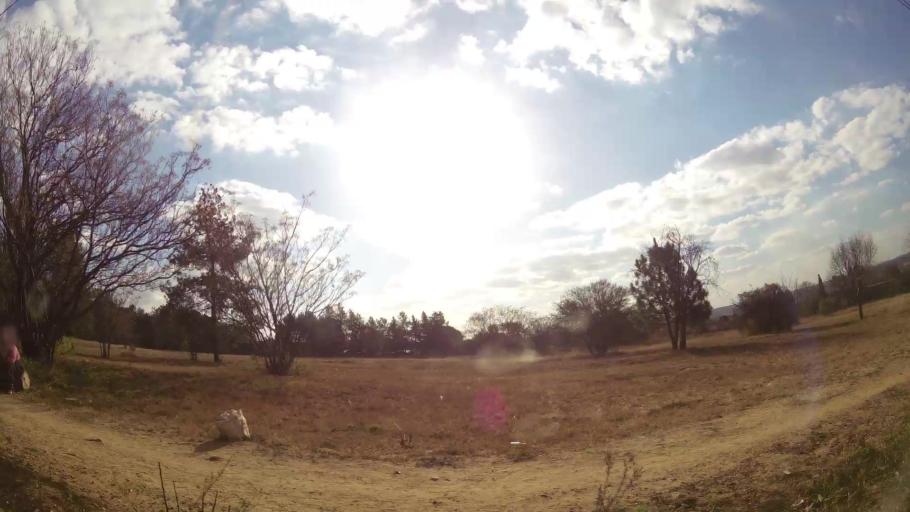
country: ZA
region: Gauteng
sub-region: City of Johannesburg Metropolitan Municipality
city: Diepsloot
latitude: -26.0038
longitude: 28.0217
